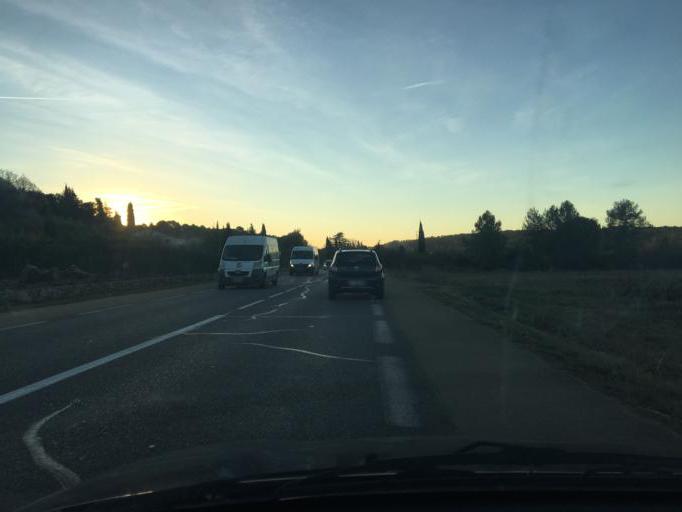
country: FR
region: Provence-Alpes-Cote d'Azur
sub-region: Departement du Var
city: Lorgues
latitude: 43.4847
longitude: 6.3678
